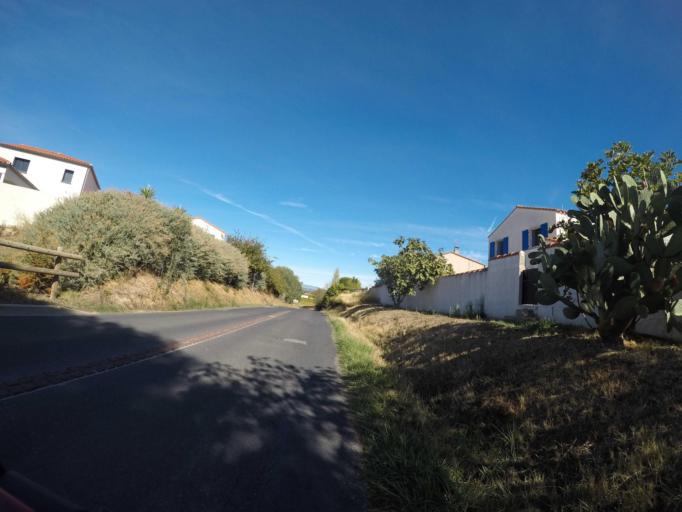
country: FR
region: Languedoc-Roussillon
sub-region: Departement des Pyrenees-Orientales
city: Ponteilla
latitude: 42.6292
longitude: 2.8117
